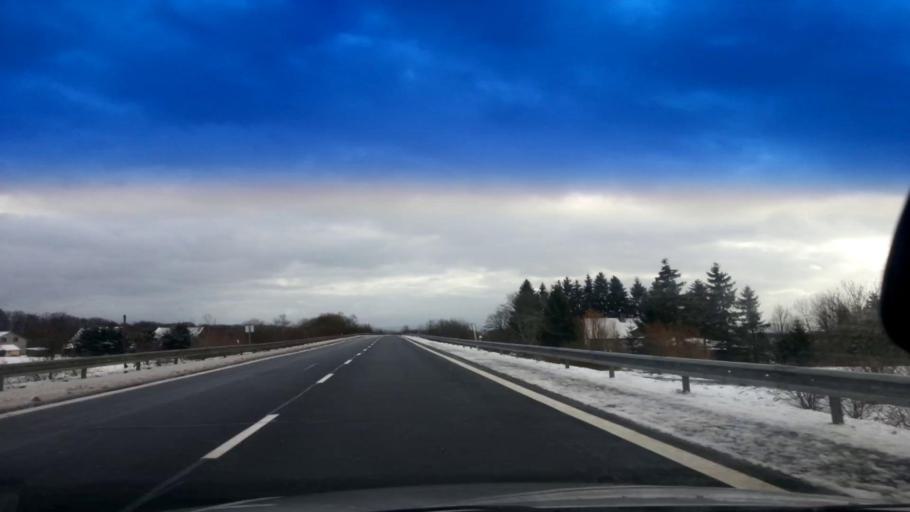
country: CZ
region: Karlovarsky
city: Hazlov
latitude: 50.1669
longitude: 12.2662
